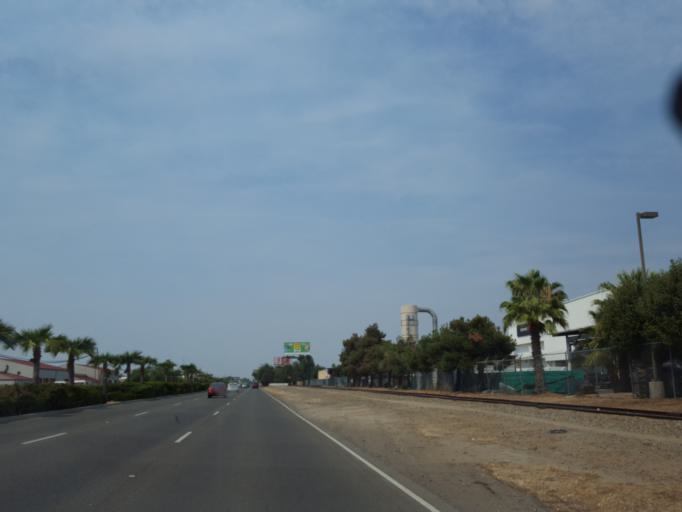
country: US
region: California
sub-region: Fresno County
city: Tarpey Village
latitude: 36.7798
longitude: -119.7001
